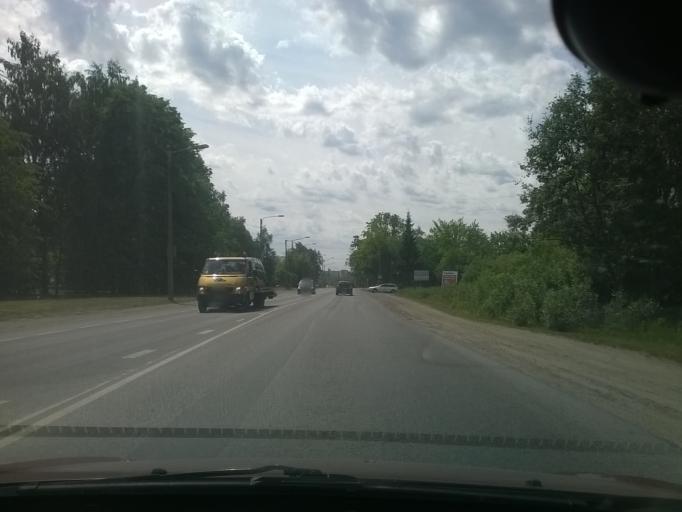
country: EE
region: Harju
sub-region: Saue vald
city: Laagri
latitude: 59.4180
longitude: 24.6373
